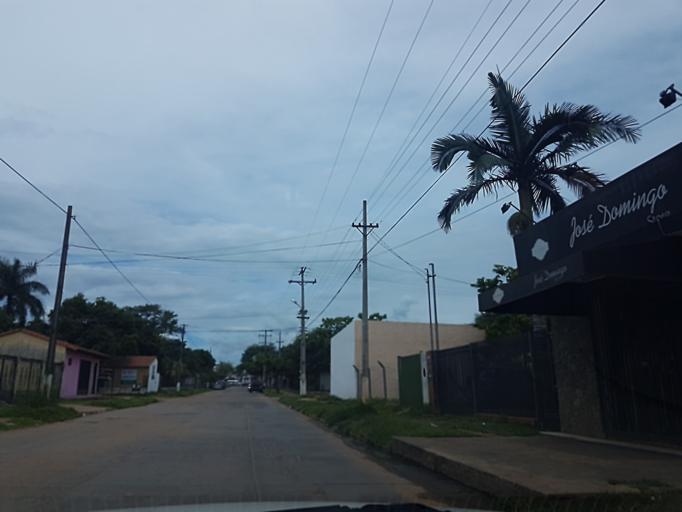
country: PY
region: Central
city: Limpio
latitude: -25.1706
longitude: -57.4779
